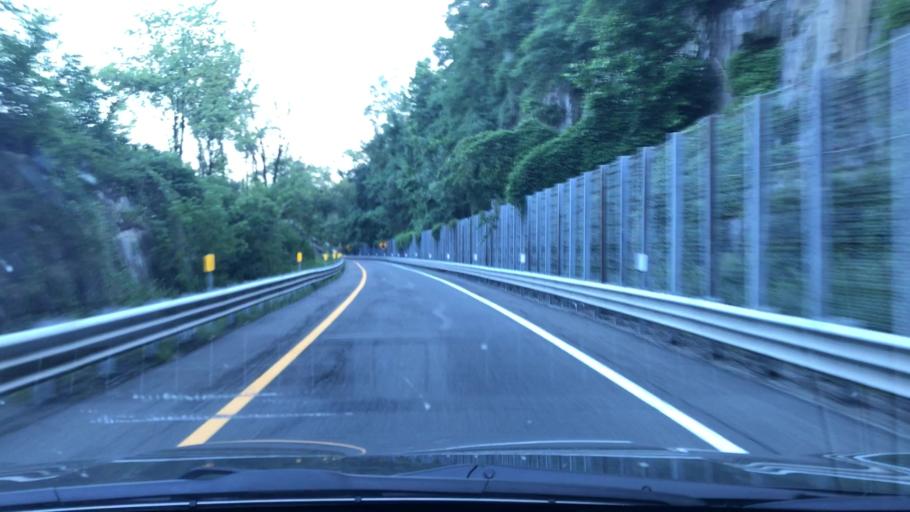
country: US
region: New York
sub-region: Westchester County
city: Greenburgh
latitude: 41.0456
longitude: -73.8357
